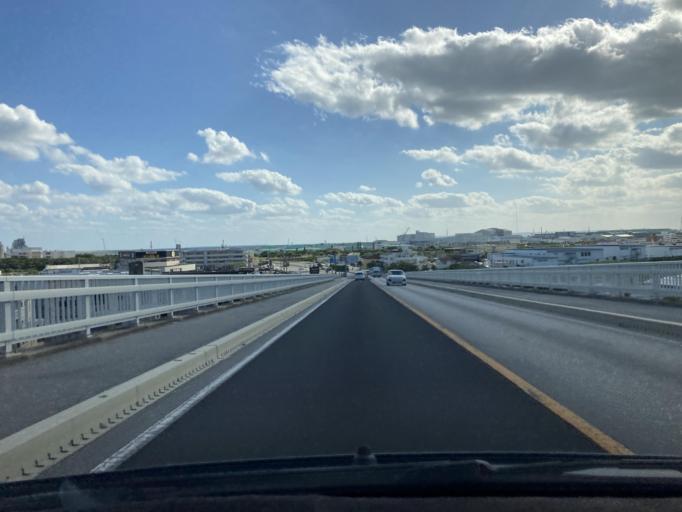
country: JP
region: Okinawa
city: Gushikawa
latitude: 26.3470
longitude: 127.8560
